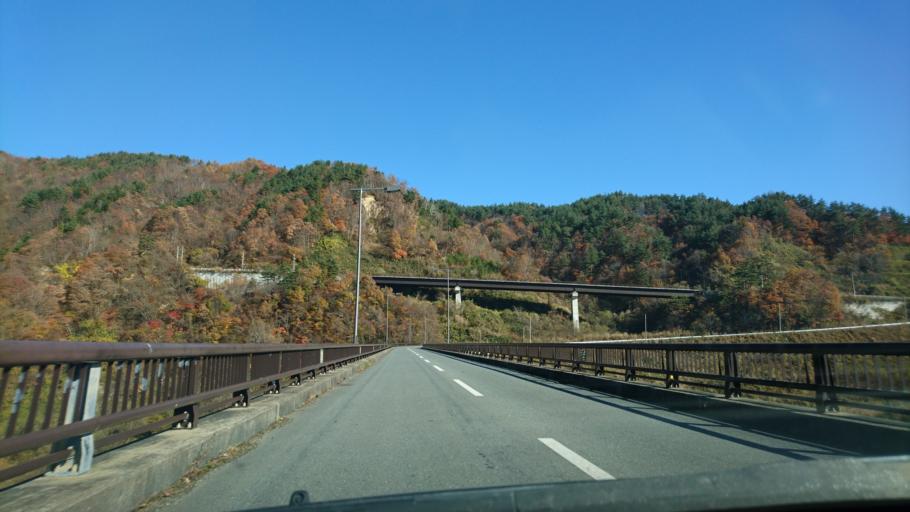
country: JP
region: Iwate
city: Mizusawa
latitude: 39.1221
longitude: 140.9340
